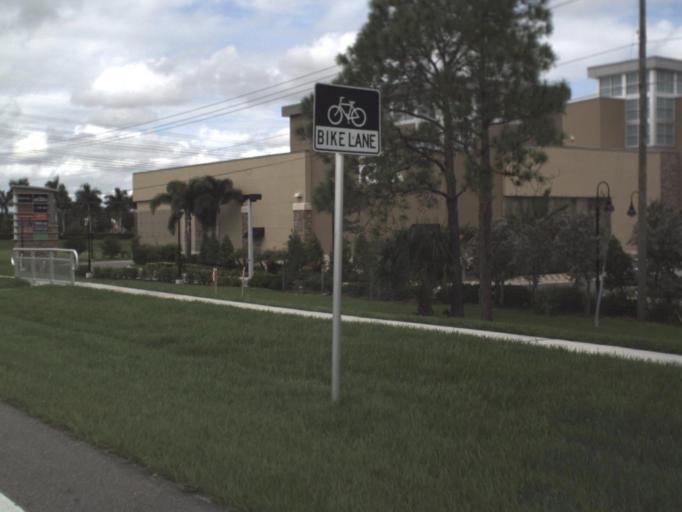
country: US
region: Florida
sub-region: Sarasota County
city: The Meadows
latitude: 27.3889
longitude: -82.4534
